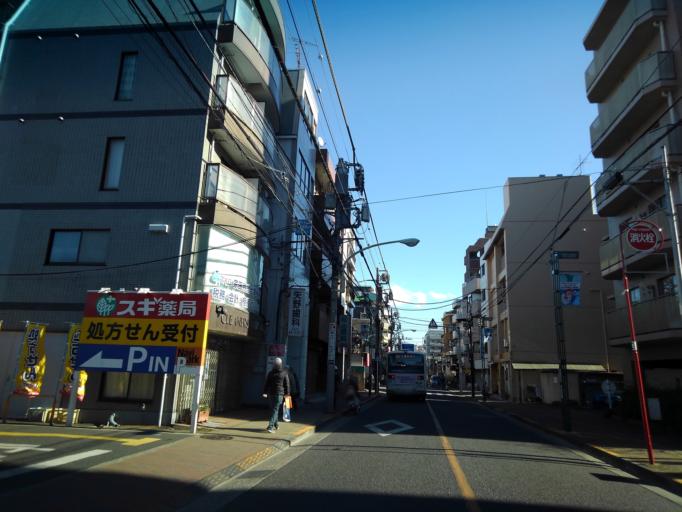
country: JP
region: Tokyo
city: Chofugaoka
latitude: 35.6518
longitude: 139.5490
